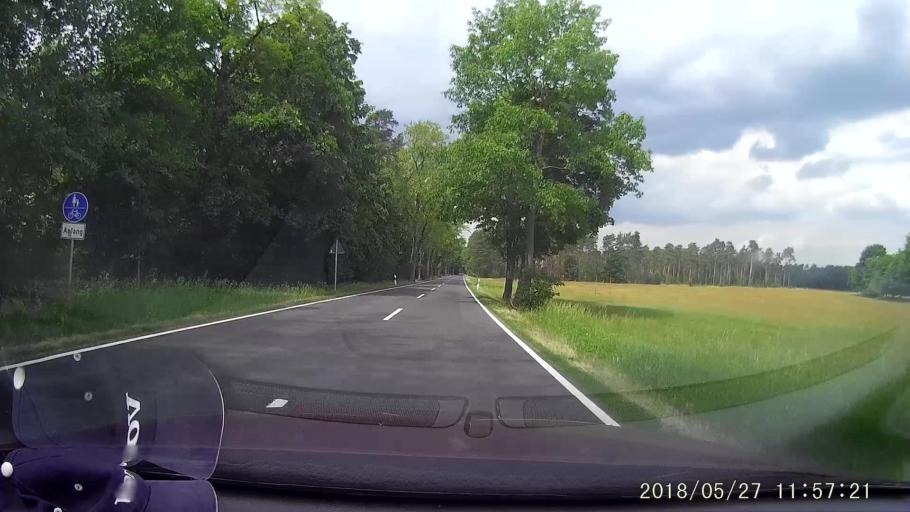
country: DE
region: Saxony
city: Mucka
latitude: 51.3045
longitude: 14.7246
